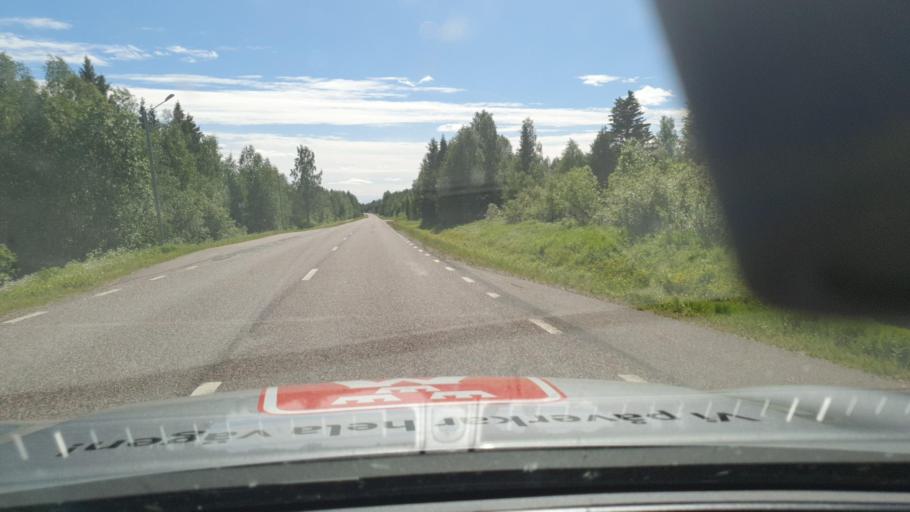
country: FI
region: Lapland
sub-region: Torniolaakso
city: Pello
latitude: 66.9404
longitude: 23.8513
